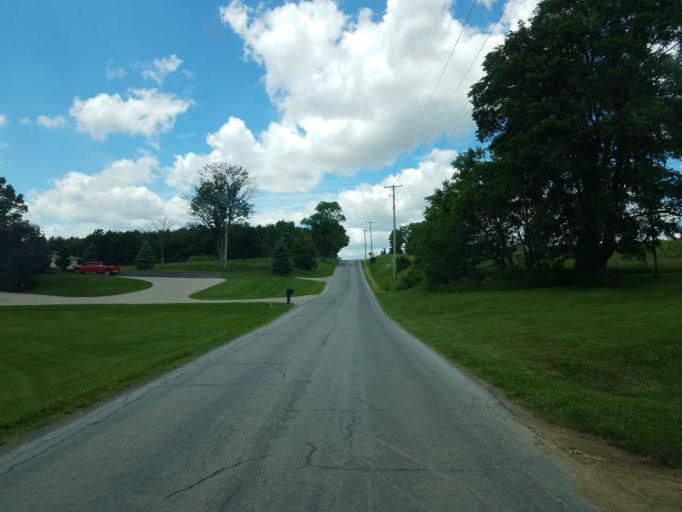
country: US
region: Ohio
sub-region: Sandusky County
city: Bellville
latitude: 40.5864
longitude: -82.5926
